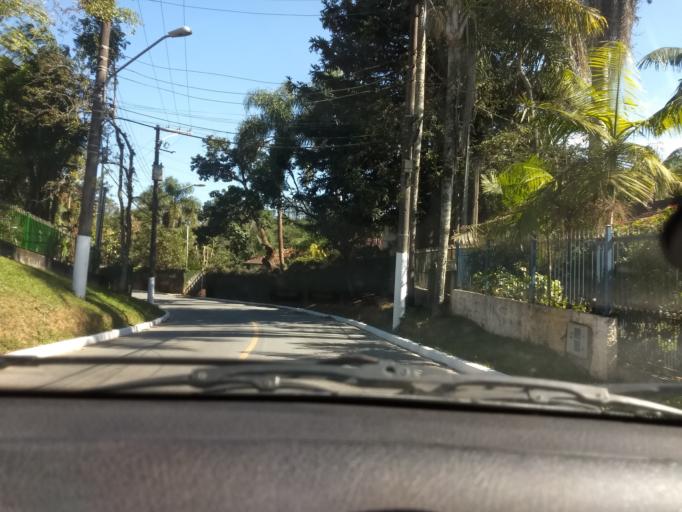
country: BR
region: Sao Paulo
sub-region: Embu-Guacu
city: Embu Guacu
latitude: -23.8037
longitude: -46.7411
